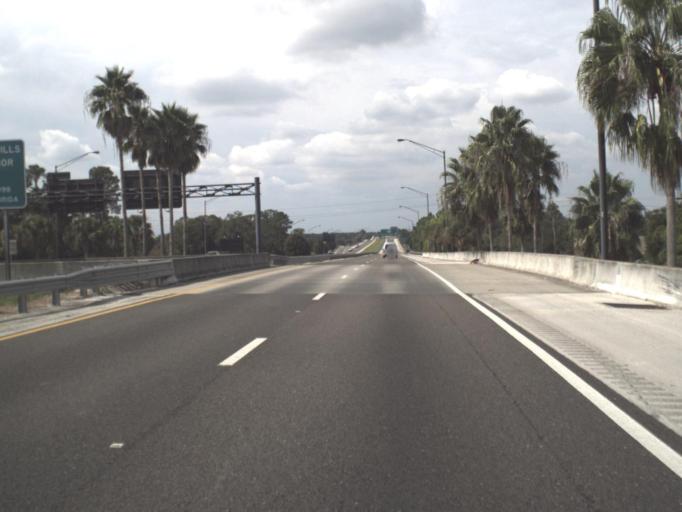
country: US
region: Florida
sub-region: Polk County
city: Medulla
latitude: 27.9965
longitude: -81.9635
